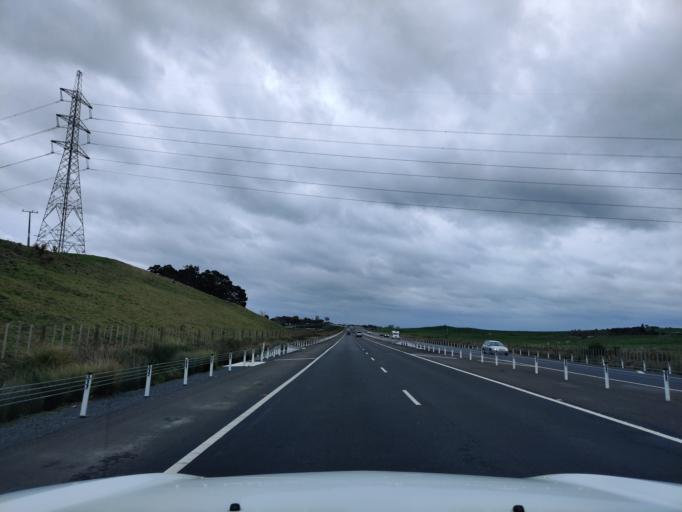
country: NZ
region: Waikato
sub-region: Waikato District
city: Te Kauwhata
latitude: -37.5183
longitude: 175.1715
